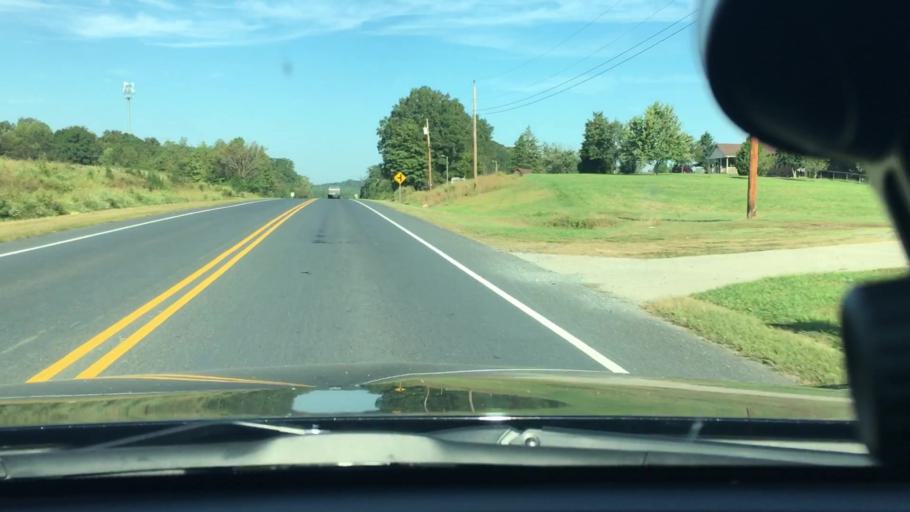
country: US
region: North Carolina
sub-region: Stanly County
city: Albemarle
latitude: 35.3797
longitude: -80.1737
